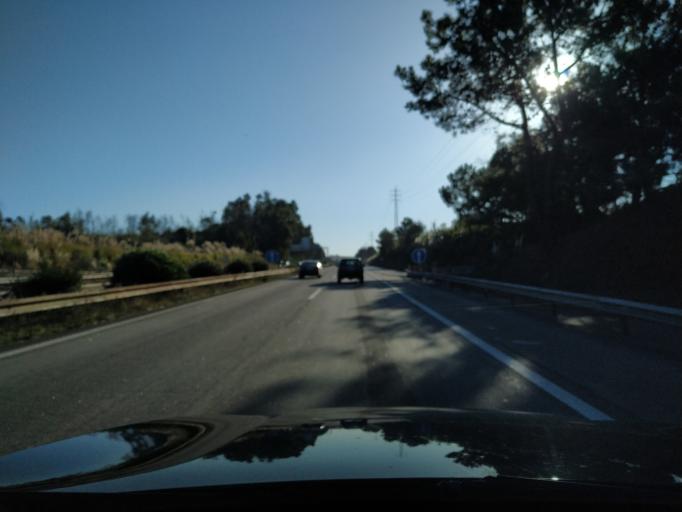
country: PT
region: Porto
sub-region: Vila Nova de Gaia
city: Vila Nova de Gaia
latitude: 41.1147
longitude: -8.6248
